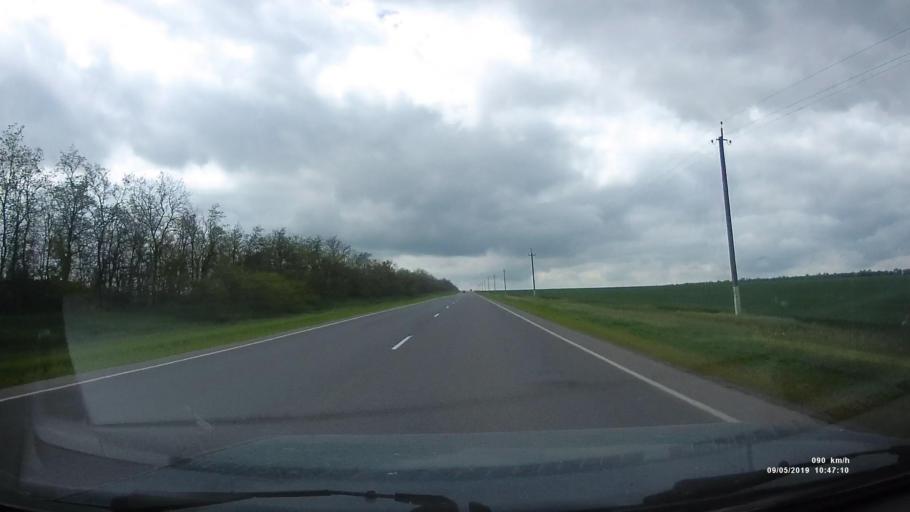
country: RU
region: Rostov
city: Peshkovo
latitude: 46.9745
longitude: 39.3557
